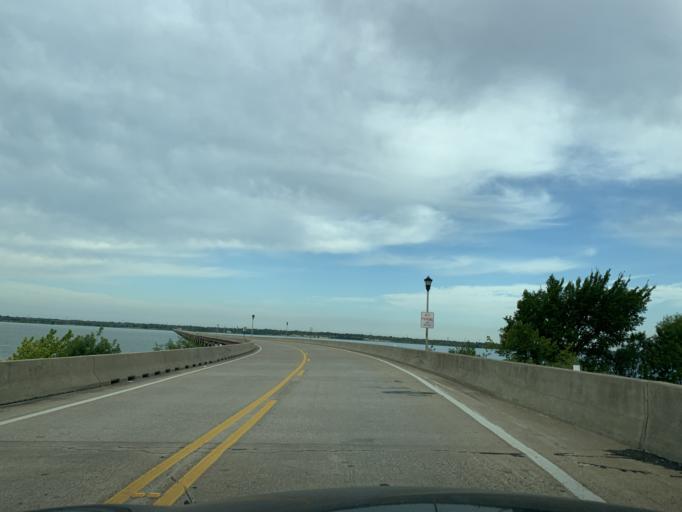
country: US
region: Texas
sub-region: Dallas County
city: Grand Prairie
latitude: 32.7079
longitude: -96.9544
